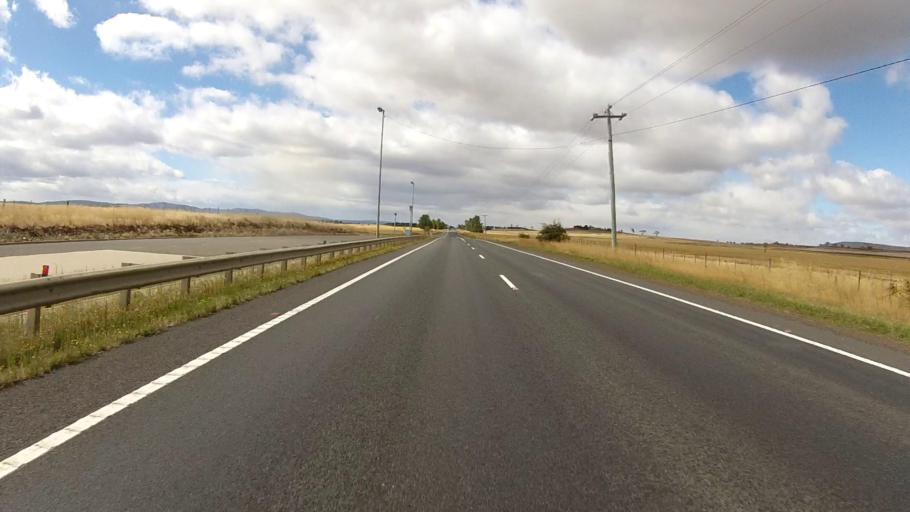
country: AU
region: Tasmania
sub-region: Northern Midlands
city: Evandale
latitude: -41.8840
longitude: 147.4667
